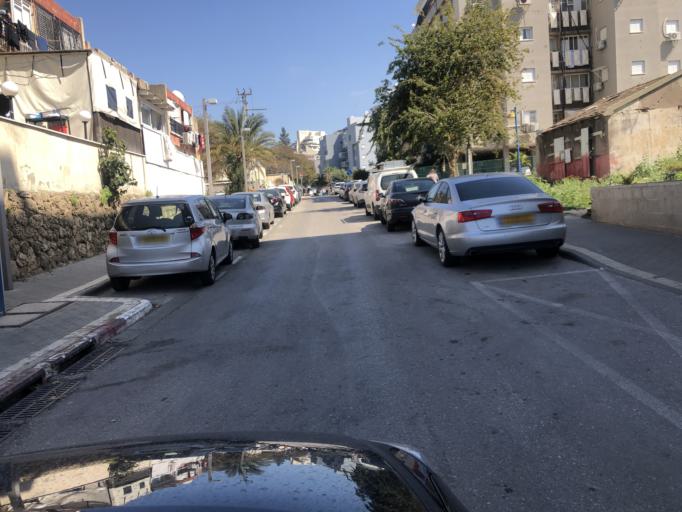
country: IL
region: Tel Aviv
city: Holon
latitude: 32.0017
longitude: 34.7637
